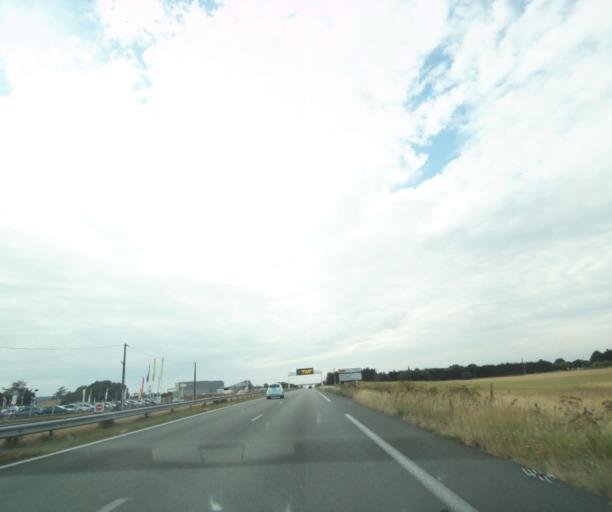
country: FR
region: Poitou-Charentes
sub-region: Departement de la Charente-Maritime
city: Angoulins
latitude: 46.0995
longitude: -1.0917
